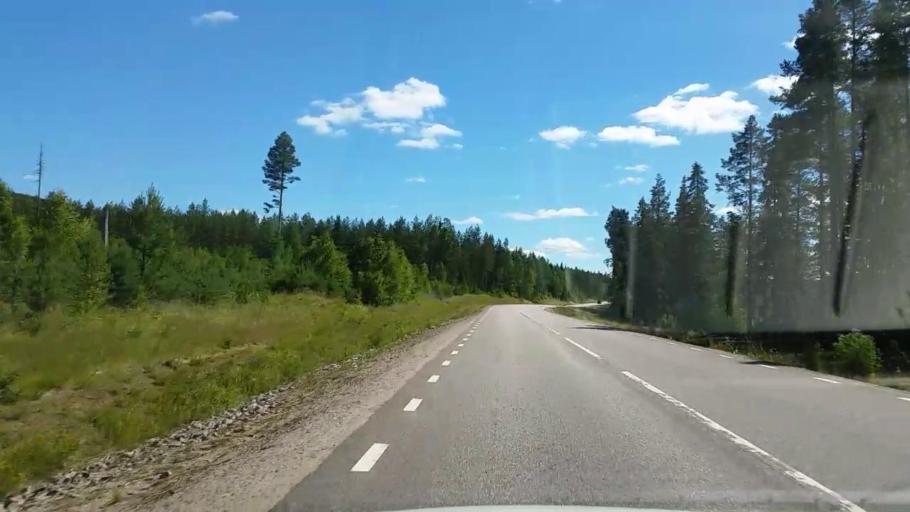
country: SE
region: Gaevleborg
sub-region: Ovanakers Kommun
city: Edsbyn
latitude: 61.1867
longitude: 15.8764
